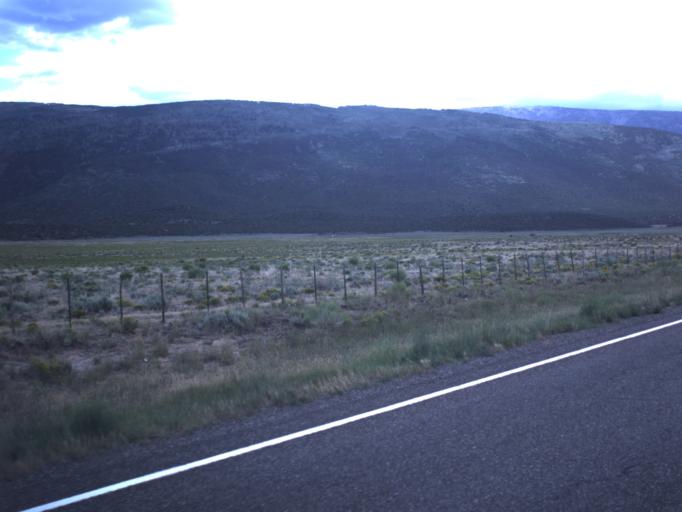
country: US
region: Utah
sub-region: Sevier County
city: Richfield
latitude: 38.6676
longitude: -111.8371
